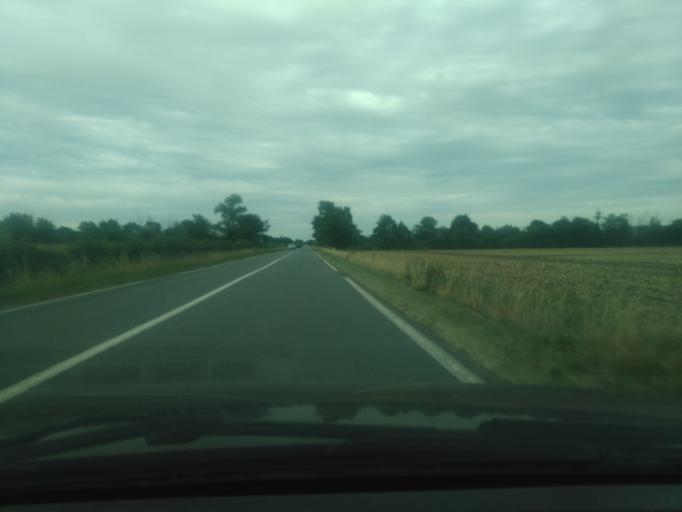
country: FR
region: Centre
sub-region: Departement du Cher
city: Charenton-du-Cher
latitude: 46.7311
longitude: 2.5982
